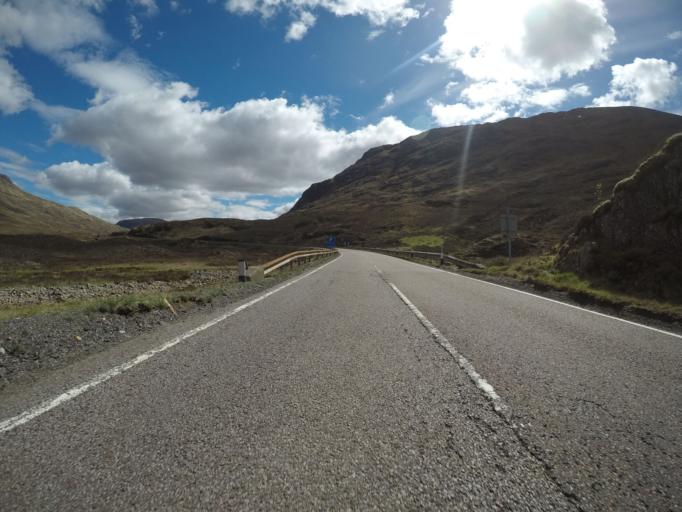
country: GB
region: Scotland
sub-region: Highland
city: Fort William
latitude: 56.6625
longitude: -4.9570
